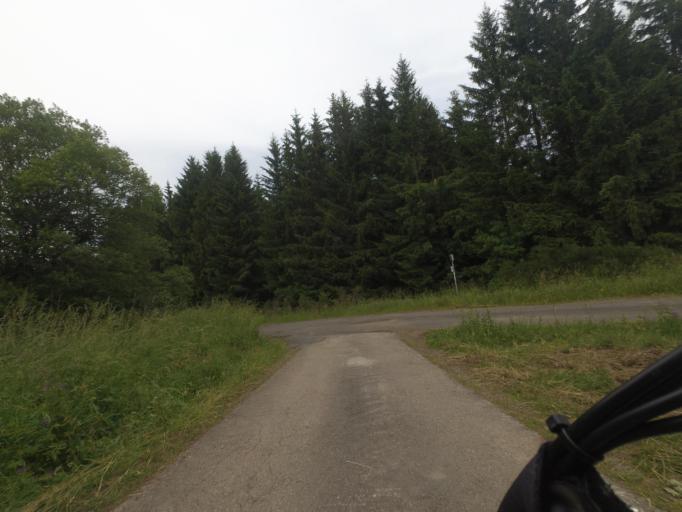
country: DE
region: Rheinland-Pfalz
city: Stadtkyll
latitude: 50.3240
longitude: 6.5459
